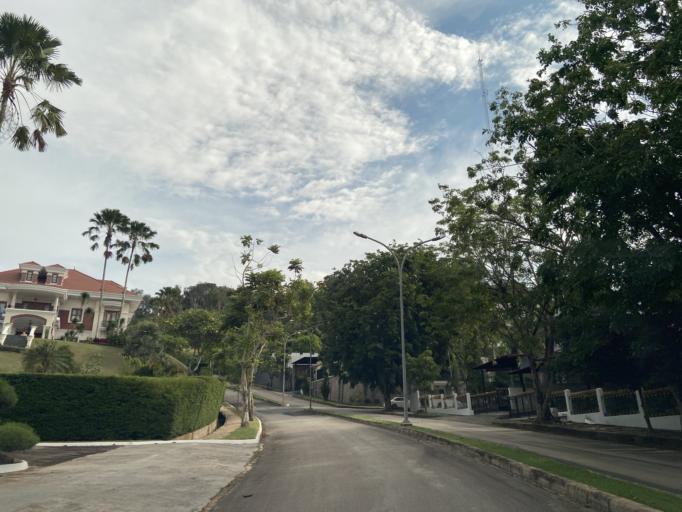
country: SG
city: Singapore
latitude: 1.1111
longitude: 104.0223
